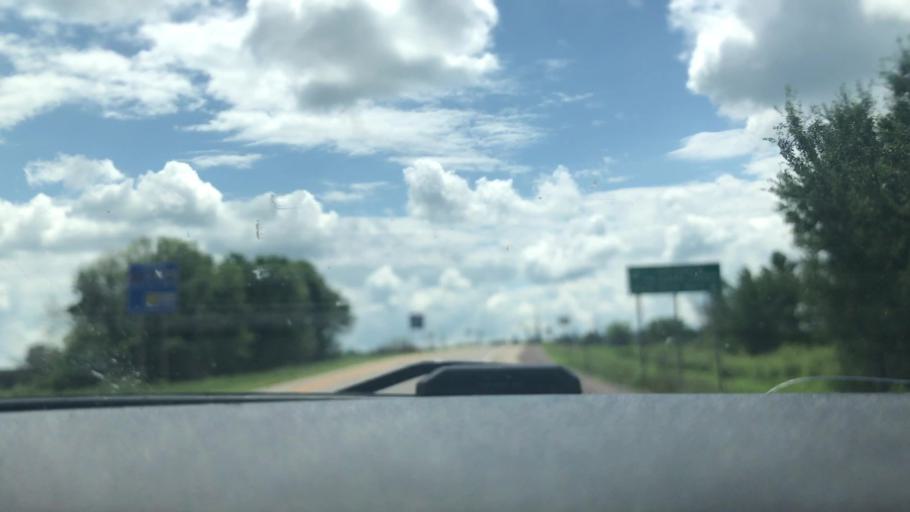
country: US
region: Wisconsin
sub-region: Jackson County
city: Black River Falls
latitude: 44.2971
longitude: -90.8252
